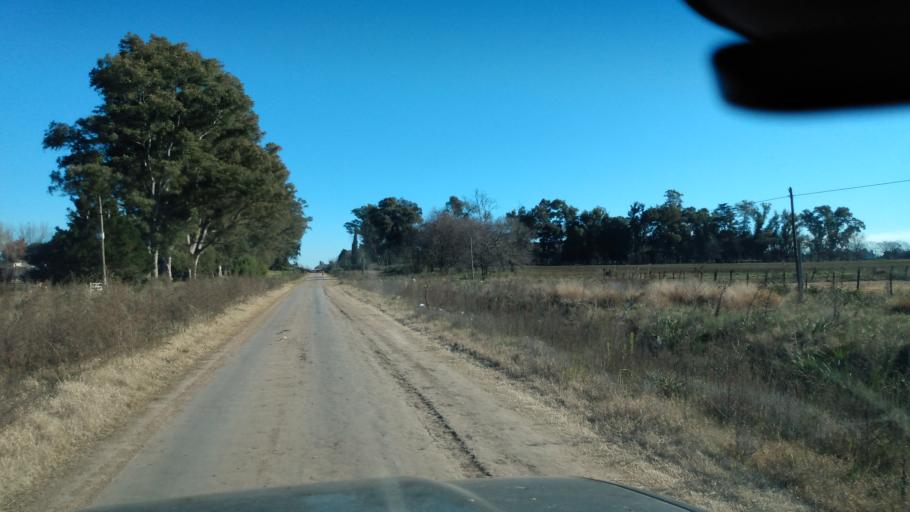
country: AR
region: Buenos Aires
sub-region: Partido de Lujan
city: Lujan
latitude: -34.5645
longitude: -59.1685
